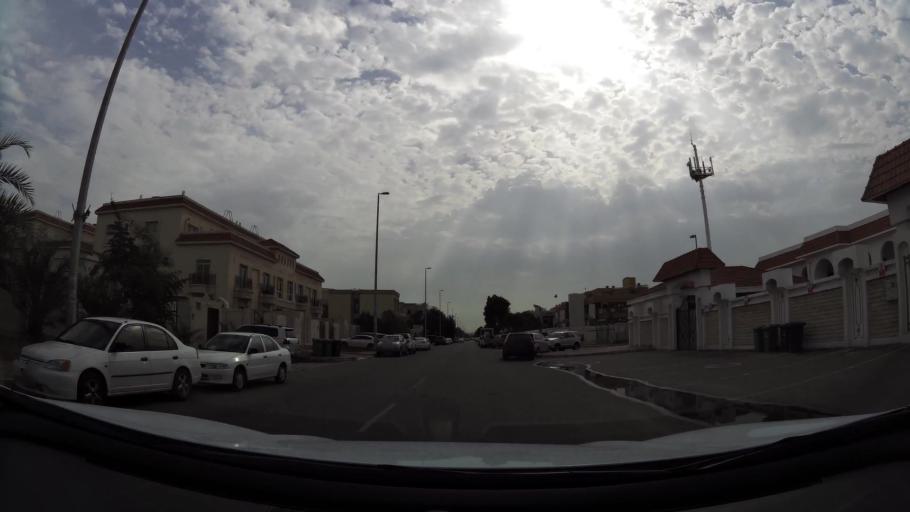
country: AE
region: Abu Dhabi
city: Abu Dhabi
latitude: 24.4463
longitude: 54.4118
